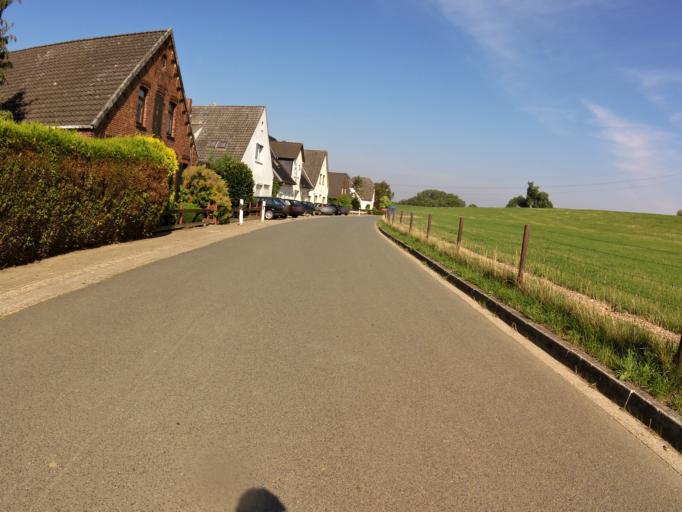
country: DE
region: Lower Saxony
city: Neuenkirchen
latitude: 53.1950
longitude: 8.5019
